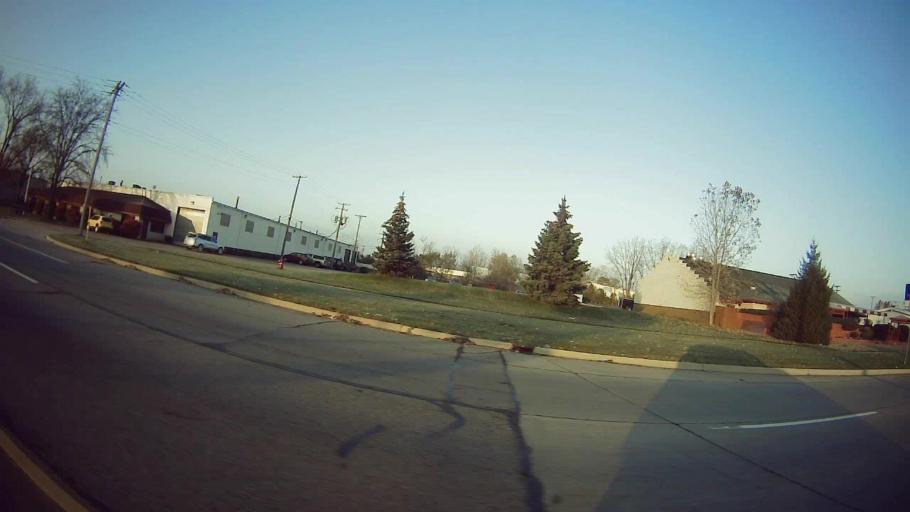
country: US
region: Michigan
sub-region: Oakland County
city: Clawson
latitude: 42.5481
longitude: -83.1076
